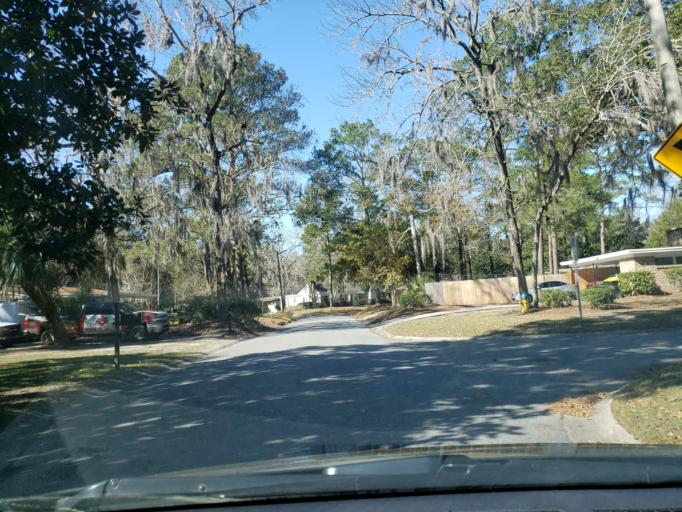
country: US
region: Georgia
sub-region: Chatham County
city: Montgomery
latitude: 31.9713
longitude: -81.1368
